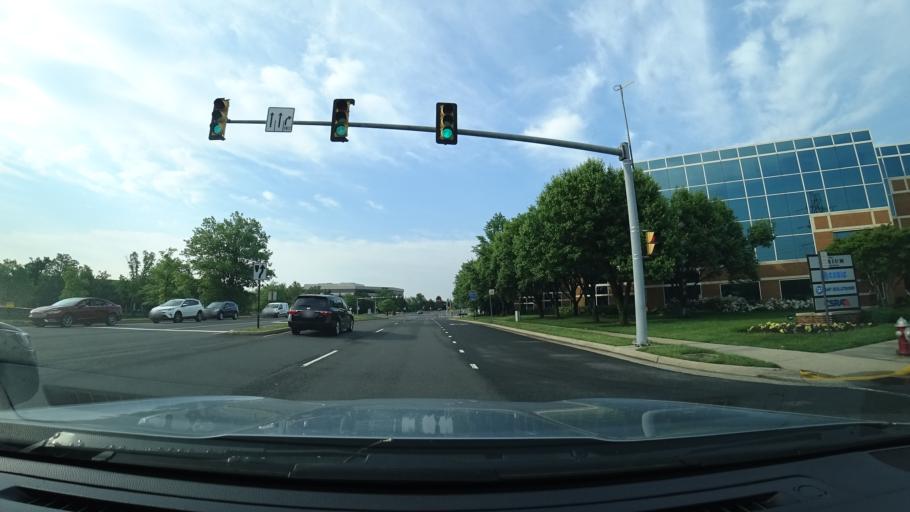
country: US
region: Virginia
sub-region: Fairfax County
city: Herndon
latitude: 38.9564
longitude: -77.3886
